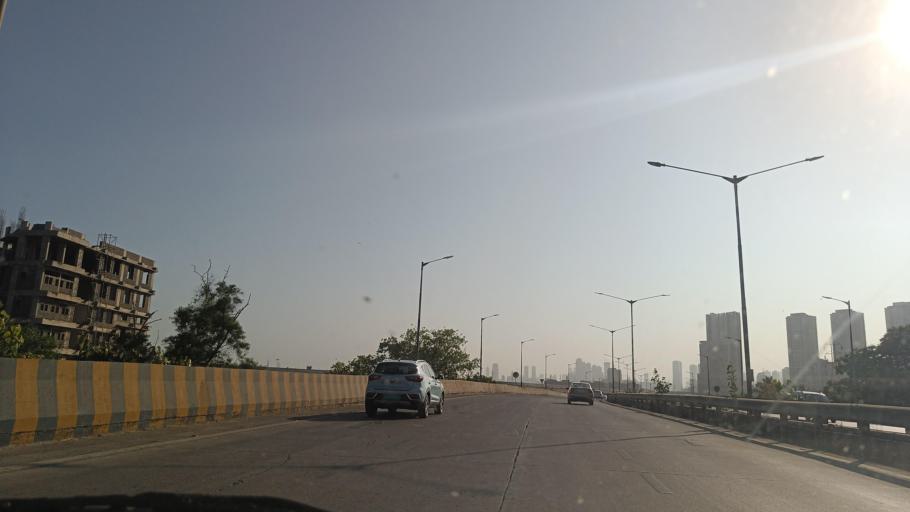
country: IN
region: Maharashtra
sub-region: Mumbai Suburban
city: Mumbai
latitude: 19.0292
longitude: 72.8890
